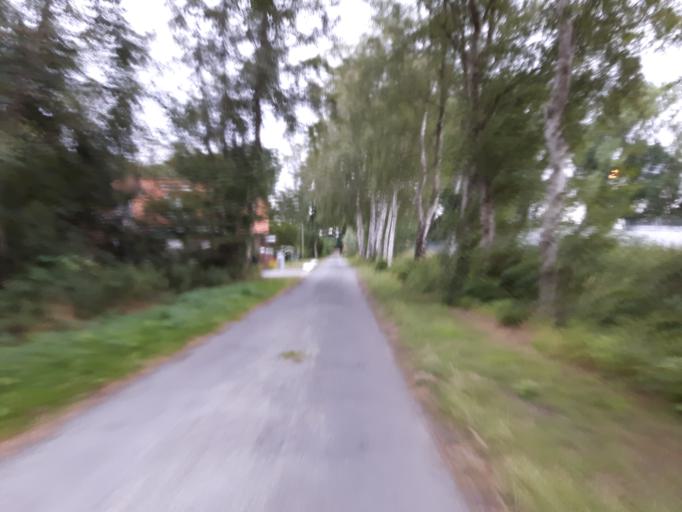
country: DE
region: Lower Saxony
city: Stuhr
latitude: 53.0193
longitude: 8.6955
